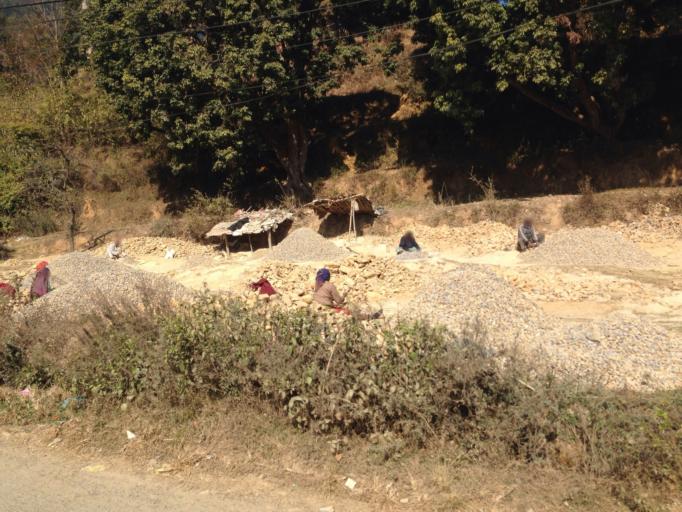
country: NP
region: Central Region
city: Kirtipur
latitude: 27.7268
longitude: 85.2689
